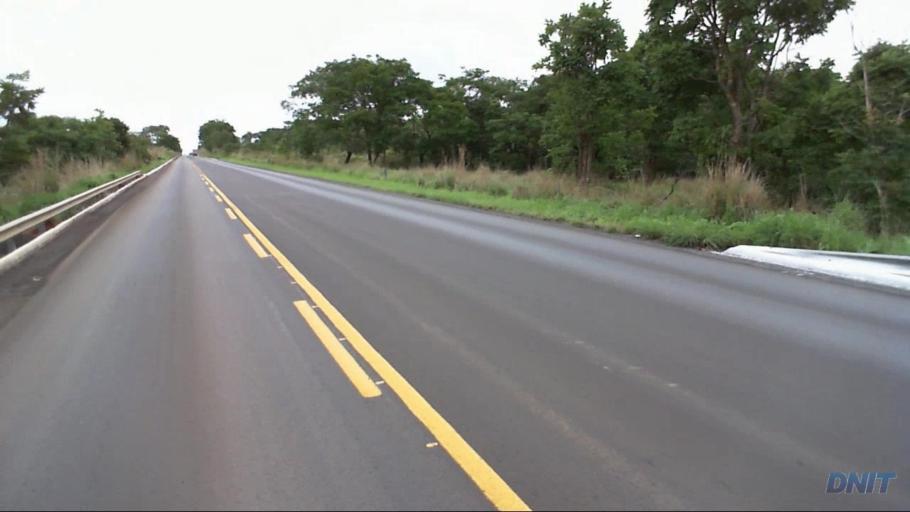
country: BR
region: Goias
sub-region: Padre Bernardo
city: Padre Bernardo
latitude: -15.1775
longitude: -48.4135
